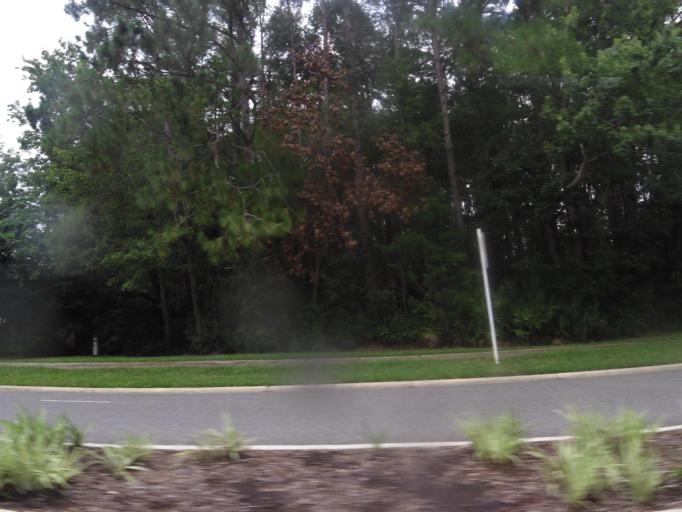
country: US
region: Florida
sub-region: Saint Johns County
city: Ponte Vedra Beach
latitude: 30.2562
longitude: -81.4570
